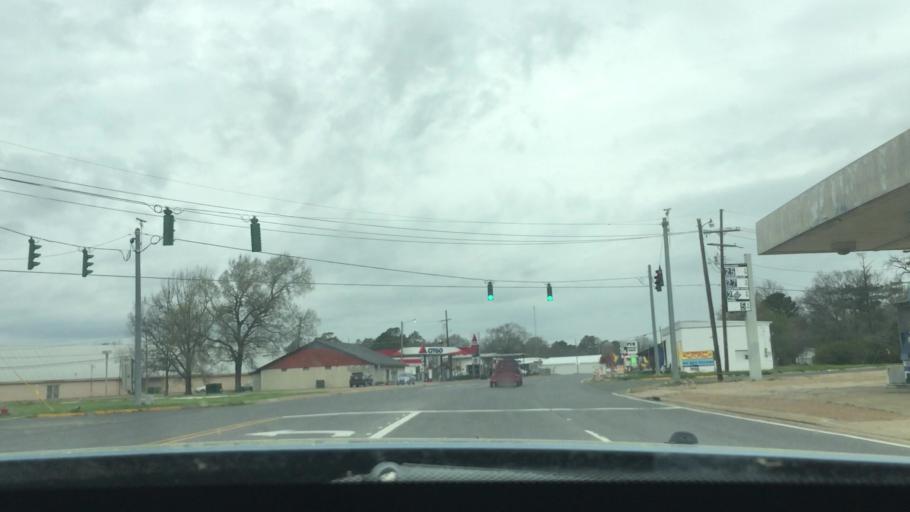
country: US
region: Louisiana
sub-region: Franklin Parish
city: Winnsboro
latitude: 32.1560
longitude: -91.7141
